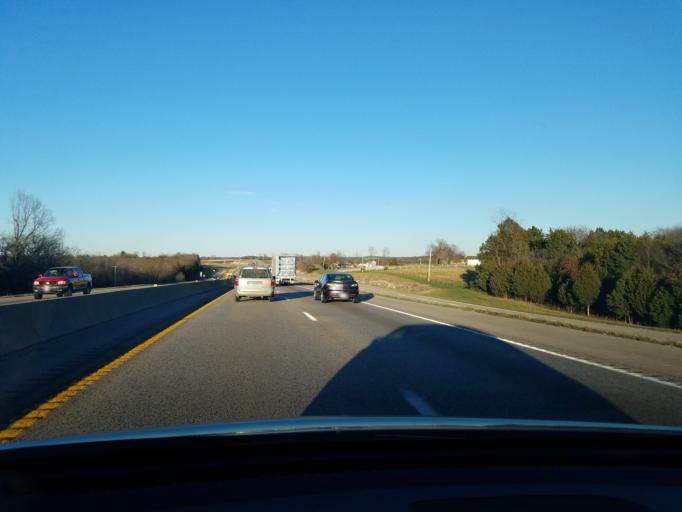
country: US
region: Missouri
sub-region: Franklin County
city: Villa Ridge
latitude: 38.4198
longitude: -90.9210
